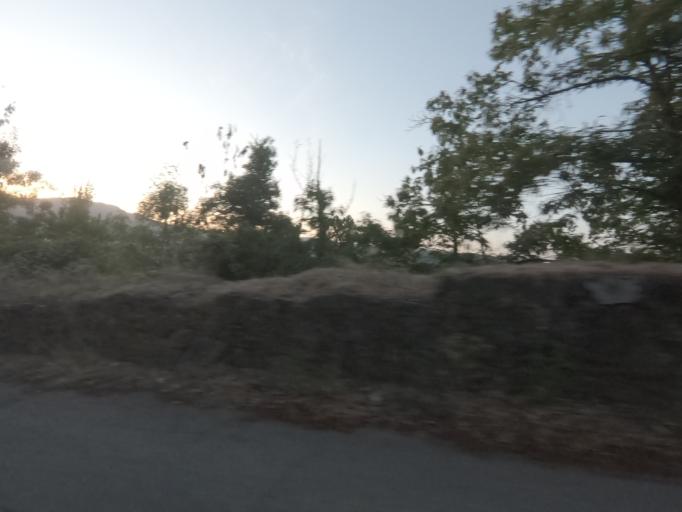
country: PT
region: Vila Real
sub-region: Peso da Regua
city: Peso da Regua
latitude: 41.1686
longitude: -7.7432
